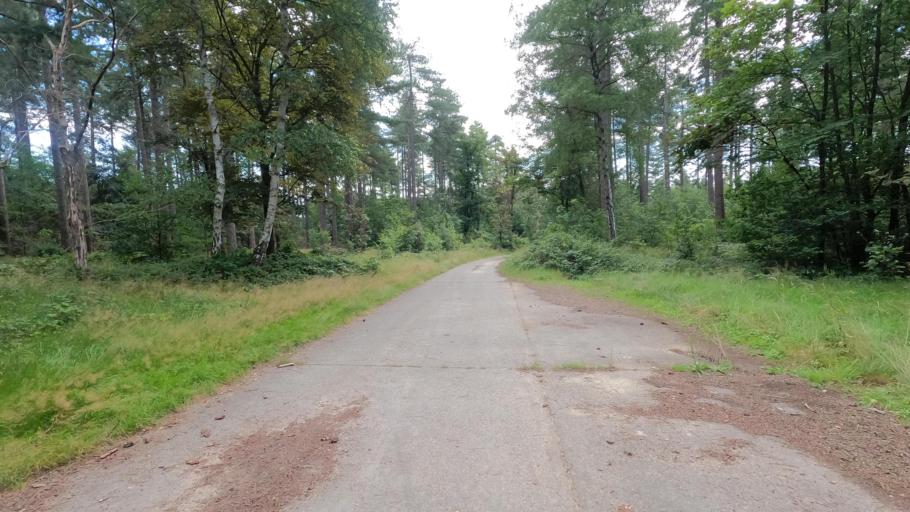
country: BE
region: Flanders
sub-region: Provincie Antwerpen
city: Oostmalle
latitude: 51.2654
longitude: 4.7606
